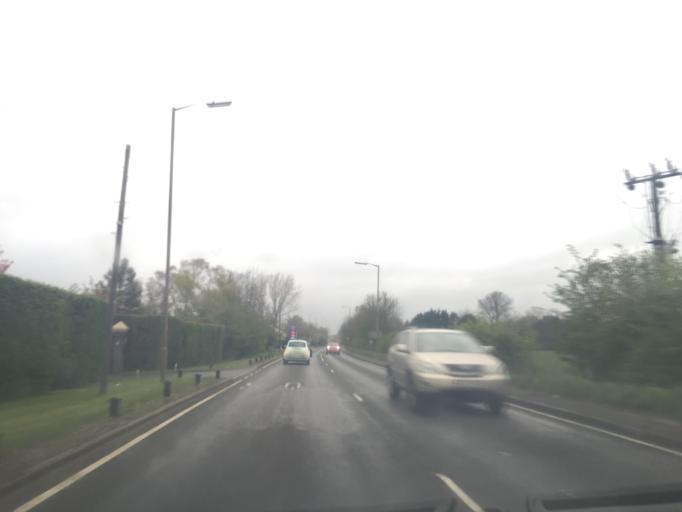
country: GB
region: England
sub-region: Essex
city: Epping
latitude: 51.7286
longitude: 0.1242
